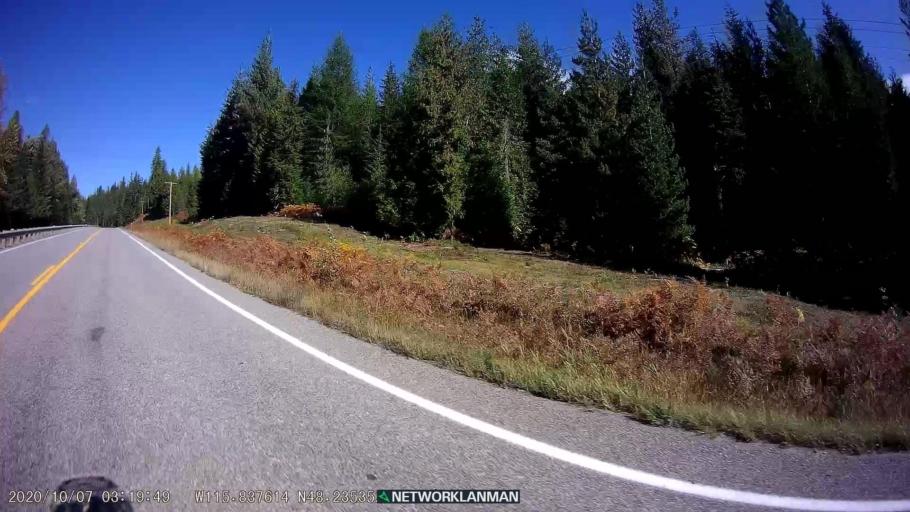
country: US
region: Montana
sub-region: Lincoln County
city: Libby
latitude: 48.2356
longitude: -115.8368
